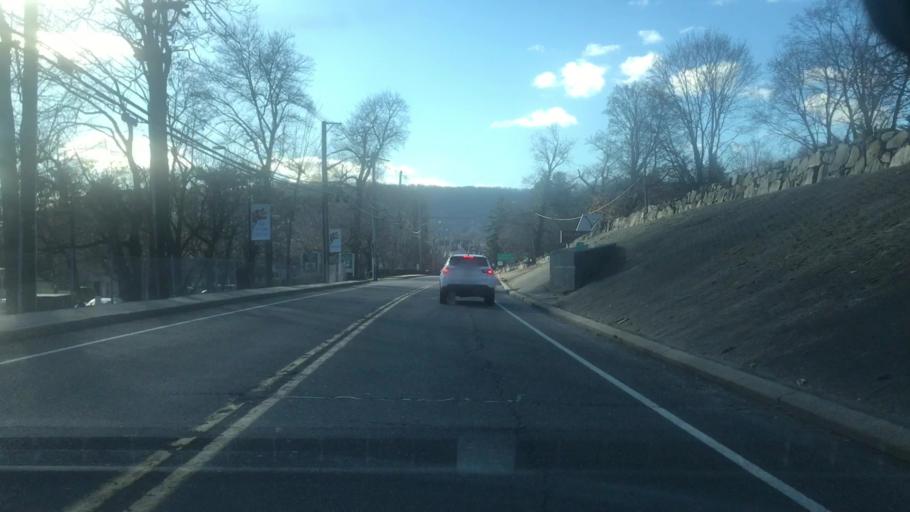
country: US
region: New York
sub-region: Rockland County
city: West Haverstraw
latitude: 41.2148
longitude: -73.9861
